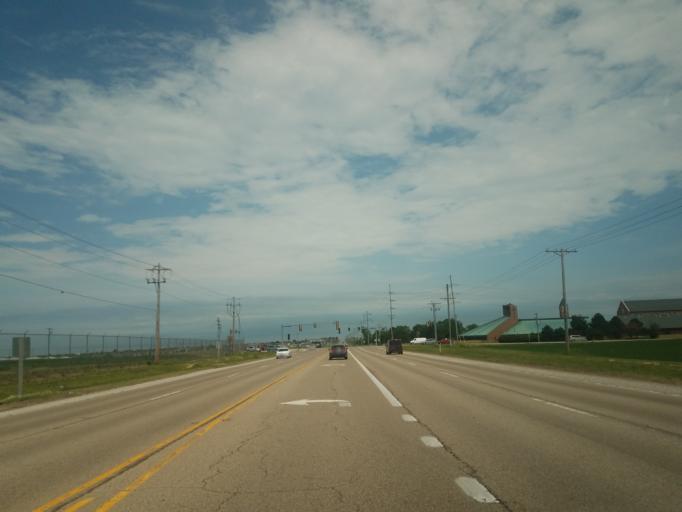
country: US
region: Illinois
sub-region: McLean County
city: Bloomington
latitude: 40.4866
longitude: -88.9025
